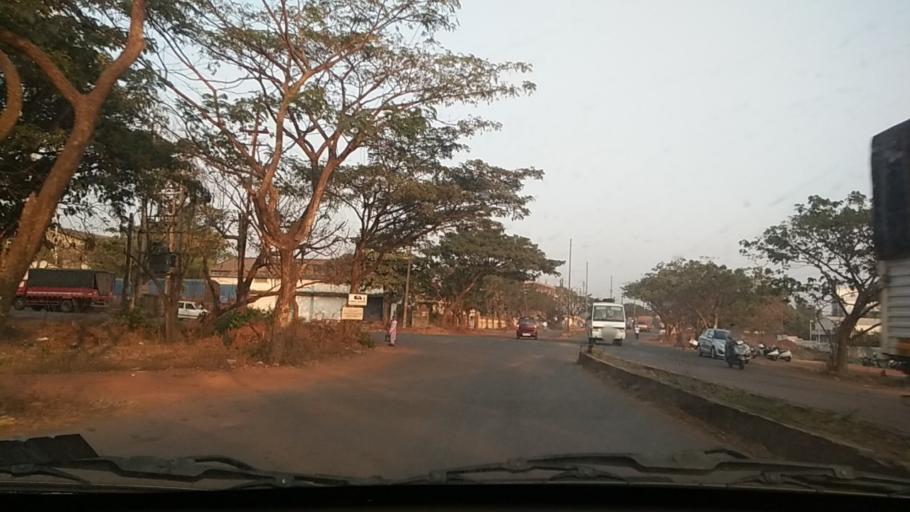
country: IN
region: Goa
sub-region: South Goa
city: Sancoale
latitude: 15.3713
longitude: 73.9304
